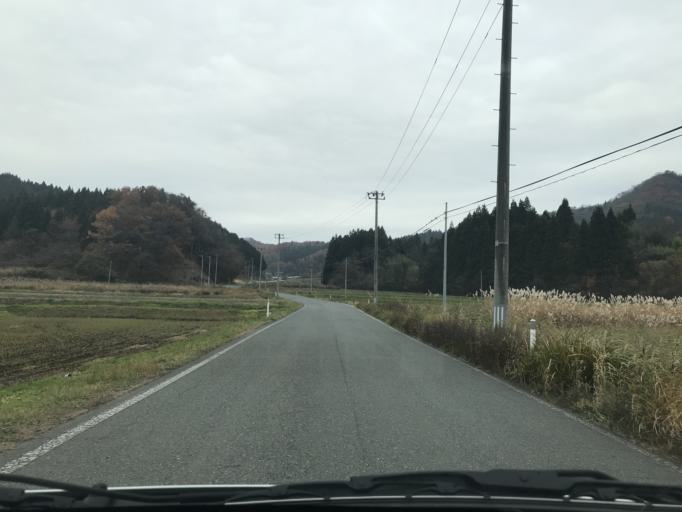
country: JP
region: Iwate
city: Kitakami
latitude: 39.2788
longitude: 141.1739
